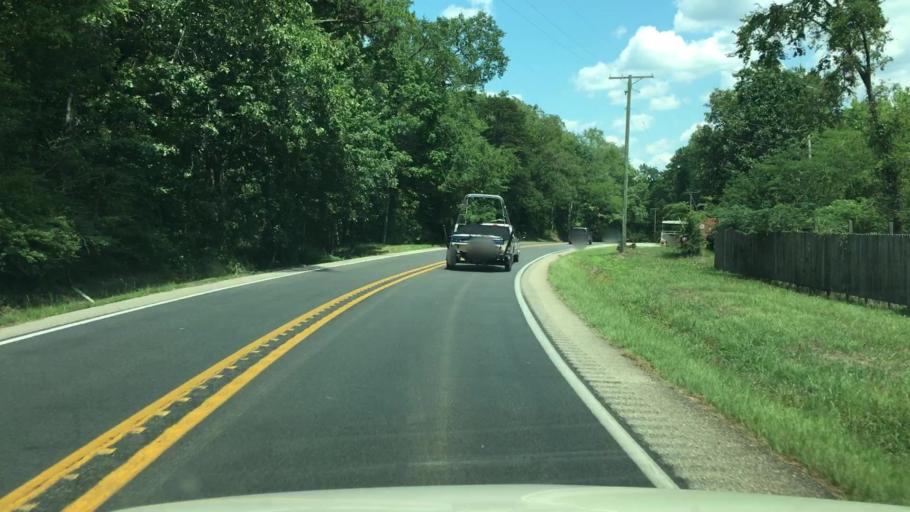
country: US
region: Arkansas
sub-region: Garland County
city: Lake Hamilton
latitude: 34.3849
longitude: -93.1294
